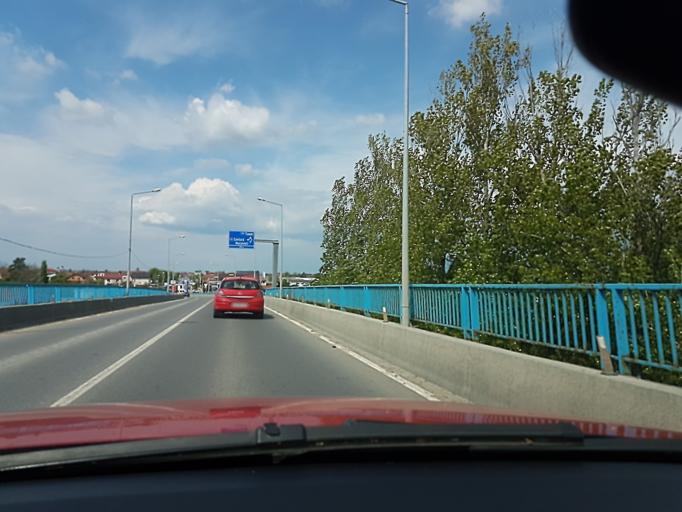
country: RO
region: Ilfov
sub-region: Comuna Tunari
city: Tunari
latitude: 44.5365
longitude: 26.1427
